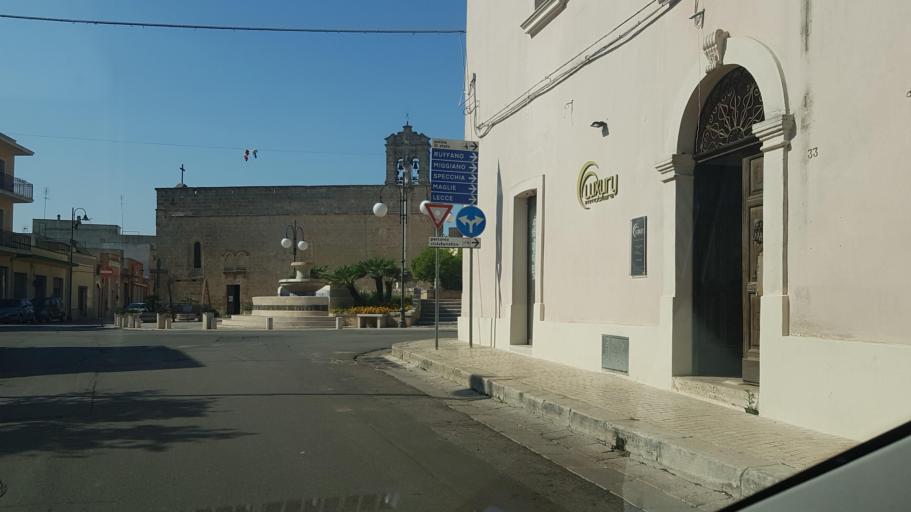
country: IT
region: Apulia
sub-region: Provincia di Lecce
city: Taurisano
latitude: 39.9576
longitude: 18.2133
